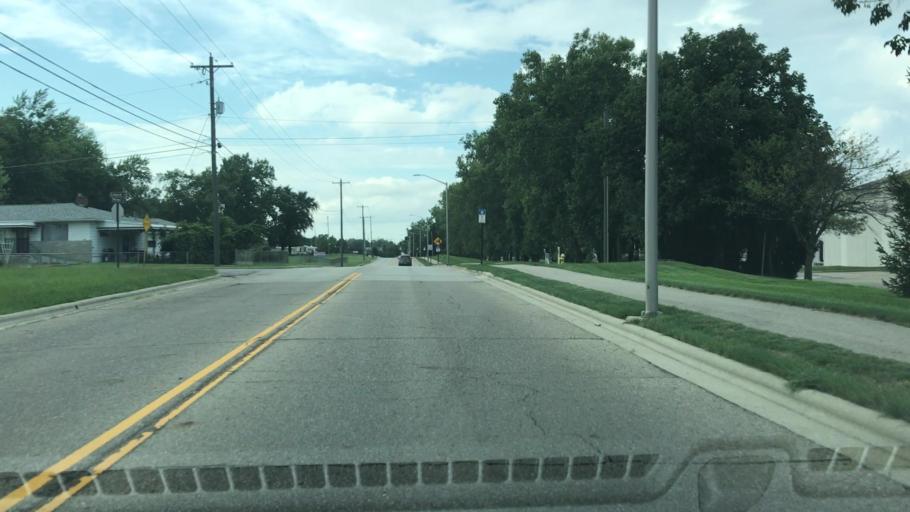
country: US
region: Ohio
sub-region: Franklin County
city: Grove City
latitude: 39.8814
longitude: -83.0602
